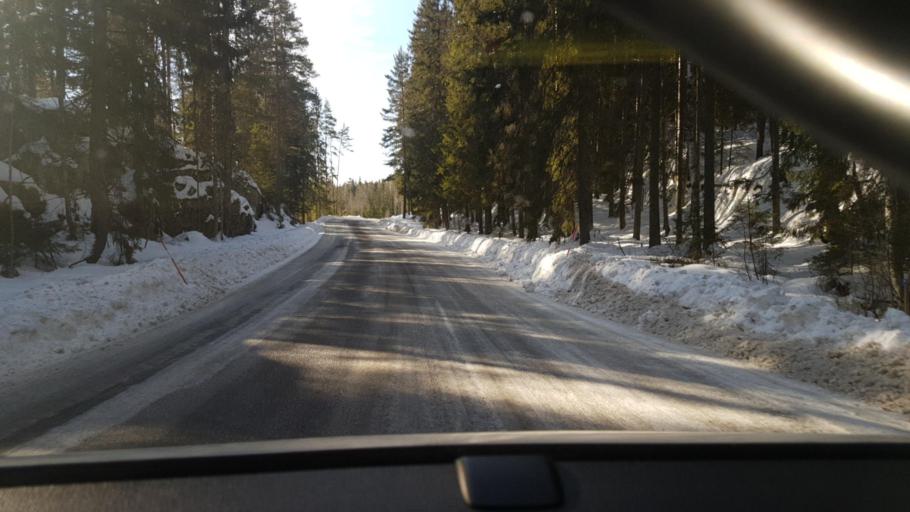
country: NO
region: Hedmark
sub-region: Eidskog
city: Skotterud
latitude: 59.8093
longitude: 12.0459
